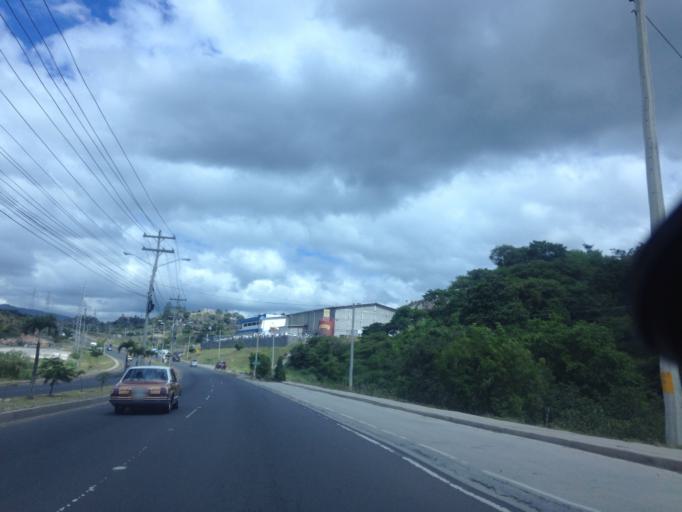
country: HN
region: Francisco Morazan
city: Yaguacire
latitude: 14.0451
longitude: -87.2423
